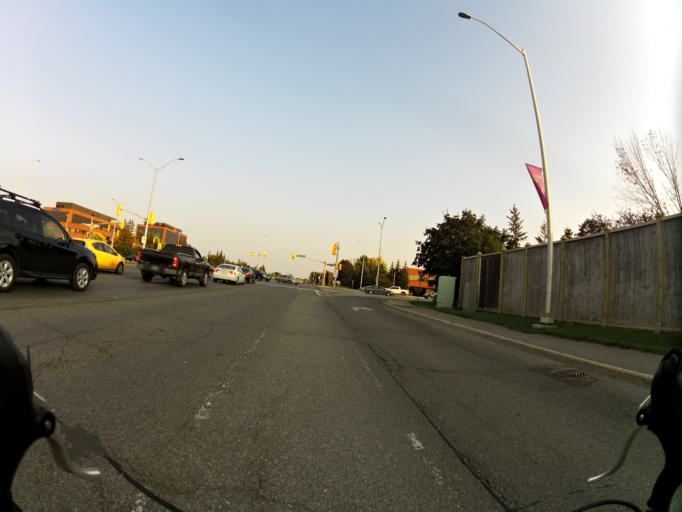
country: CA
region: Ontario
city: Bells Corners
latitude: 45.3493
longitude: -75.9255
